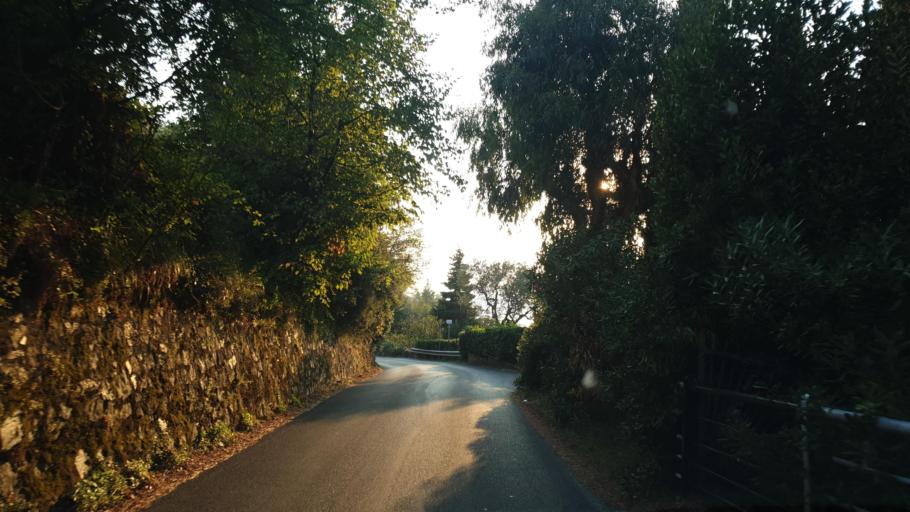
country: IT
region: Liguria
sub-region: Provincia di La Spezia
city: Bonassola
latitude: 44.1793
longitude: 9.5886
